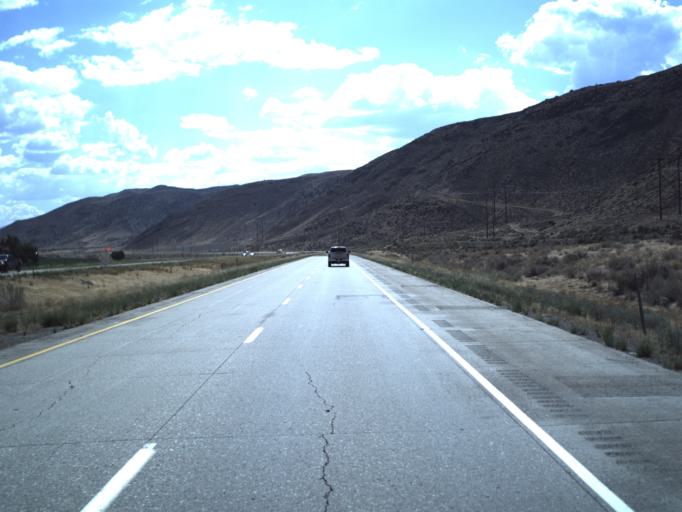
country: US
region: Utah
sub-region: Sevier County
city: Richfield
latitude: 38.7328
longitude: -112.1198
